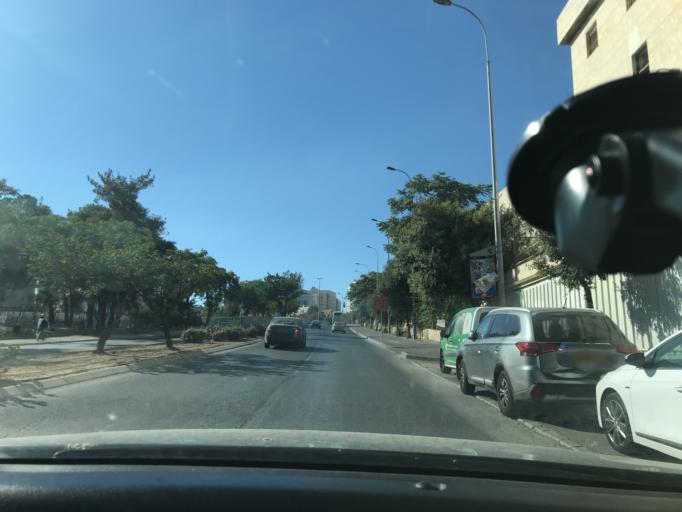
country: IL
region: Jerusalem
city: West Jerusalem
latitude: 31.7847
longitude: 35.2080
